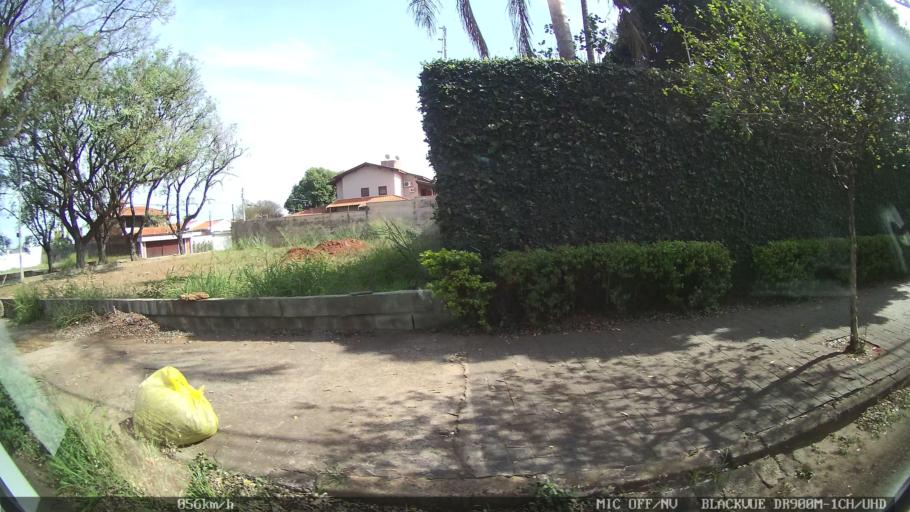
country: BR
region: Sao Paulo
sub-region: Piracicaba
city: Piracicaba
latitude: -22.7195
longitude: -47.6629
